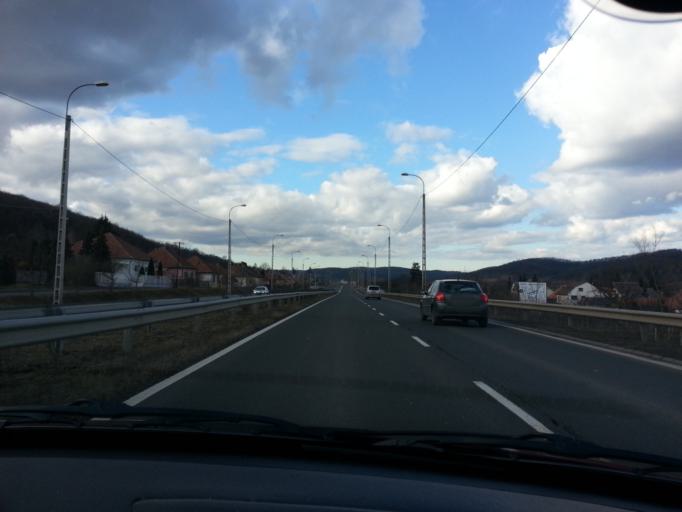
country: HU
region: Nograd
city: Kazar
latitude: 48.0338
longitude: 19.8052
